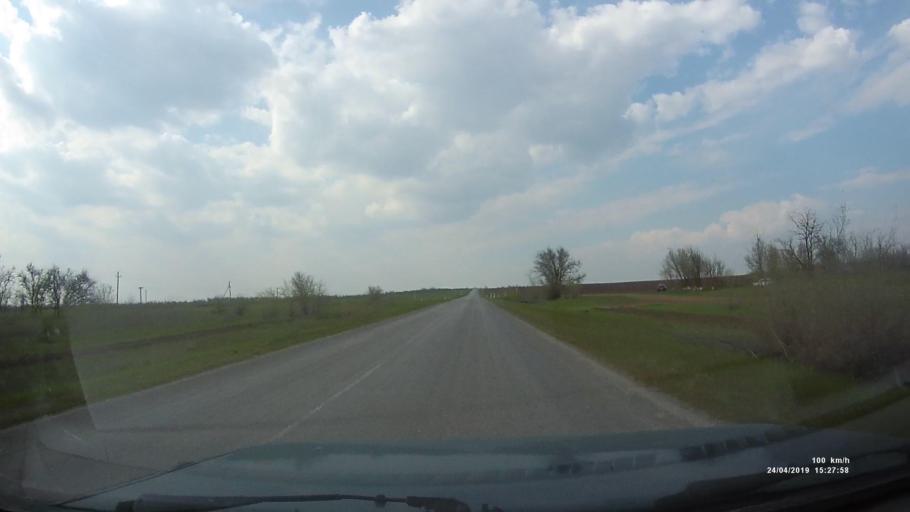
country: RU
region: Rostov
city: Remontnoye
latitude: 46.5723
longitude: 43.0219
